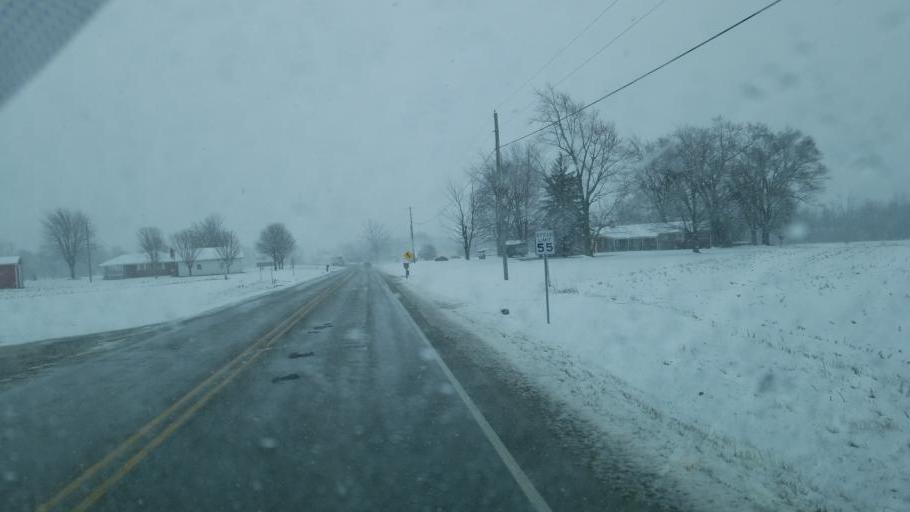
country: US
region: Indiana
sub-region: Wayne County
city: Hagerstown
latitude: 40.0220
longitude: -85.1881
